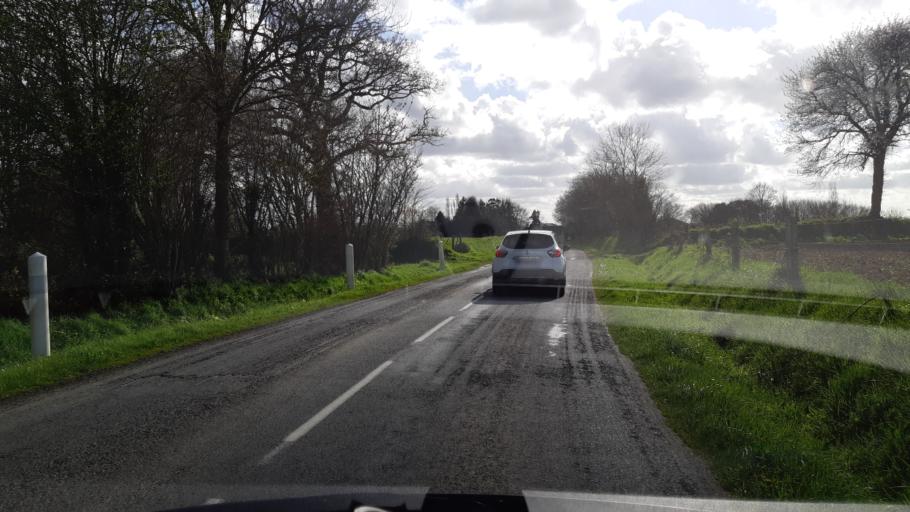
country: FR
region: Lower Normandy
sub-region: Departement de la Manche
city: Percy
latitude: 49.0160
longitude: -1.1641
